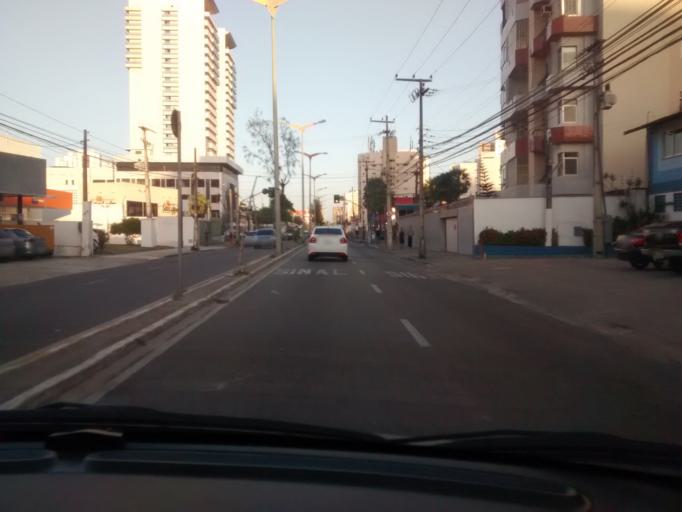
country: BR
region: Ceara
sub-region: Fortaleza
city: Fortaleza
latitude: -3.7415
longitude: -38.4822
